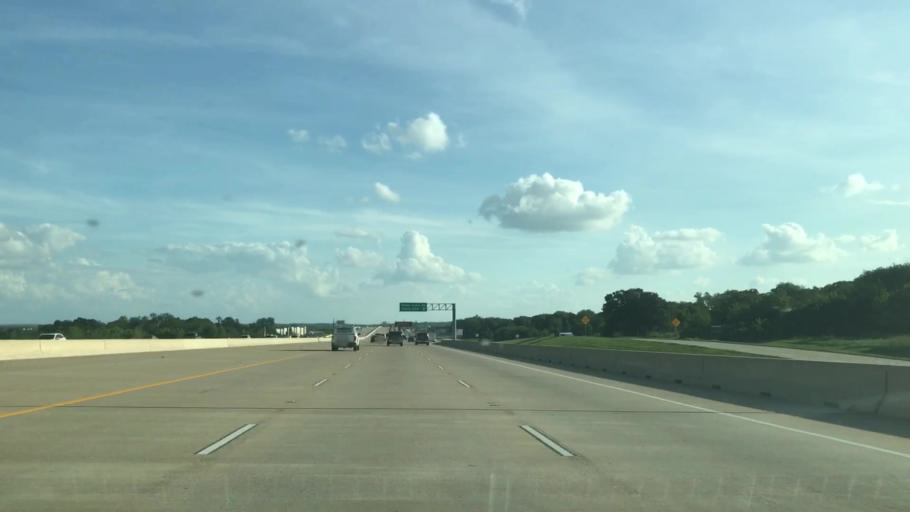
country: US
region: Texas
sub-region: Dallas County
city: Grand Prairie
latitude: 32.8104
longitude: -97.0187
